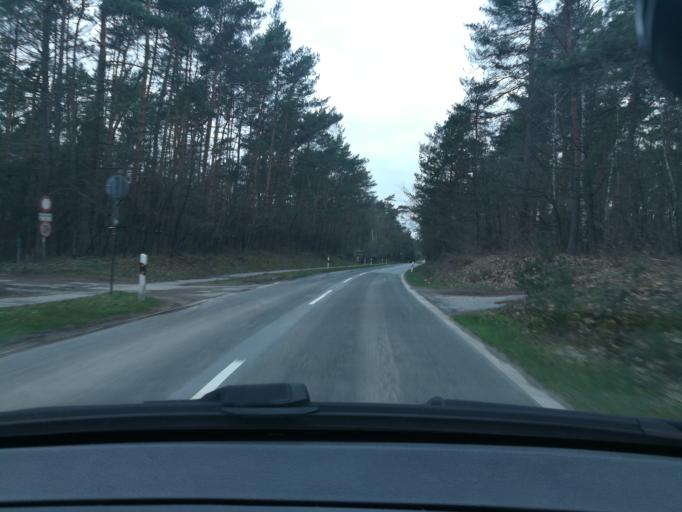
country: DE
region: North Rhine-Westphalia
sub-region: Regierungsbezirk Detmold
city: Oerlinghausen
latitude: 51.9492
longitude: 8.6271
